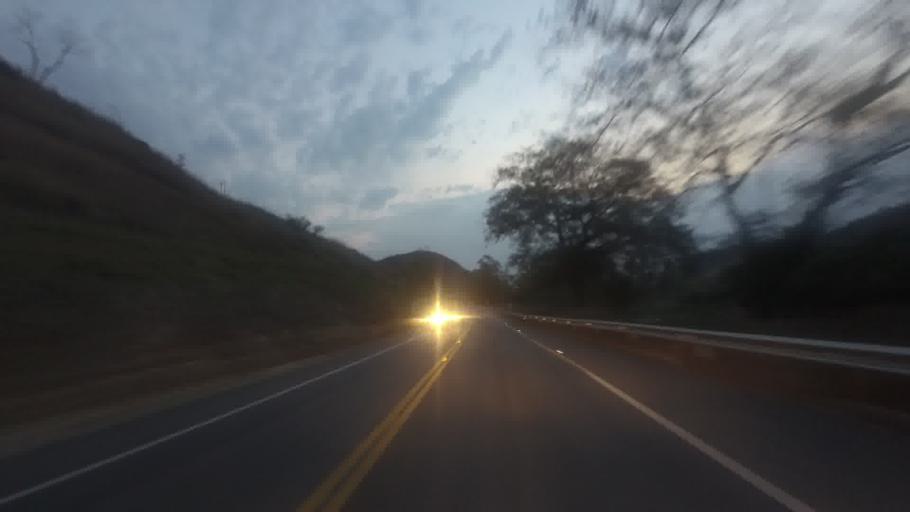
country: BR
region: Minas Gerais
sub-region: Alem Paraiba
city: Alem Paraiba
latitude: -21.9089
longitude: -42.7384
